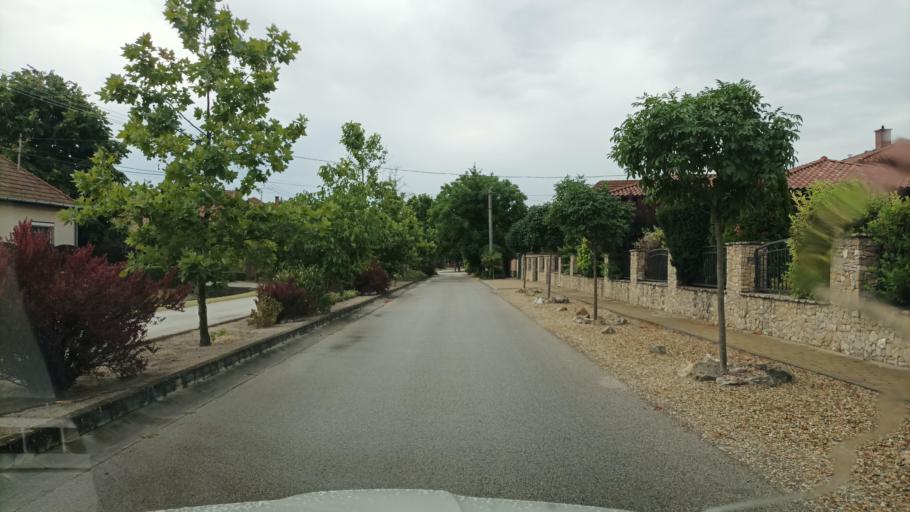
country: HU
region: Pest
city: Dabas
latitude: 47.2131
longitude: 19.2770
